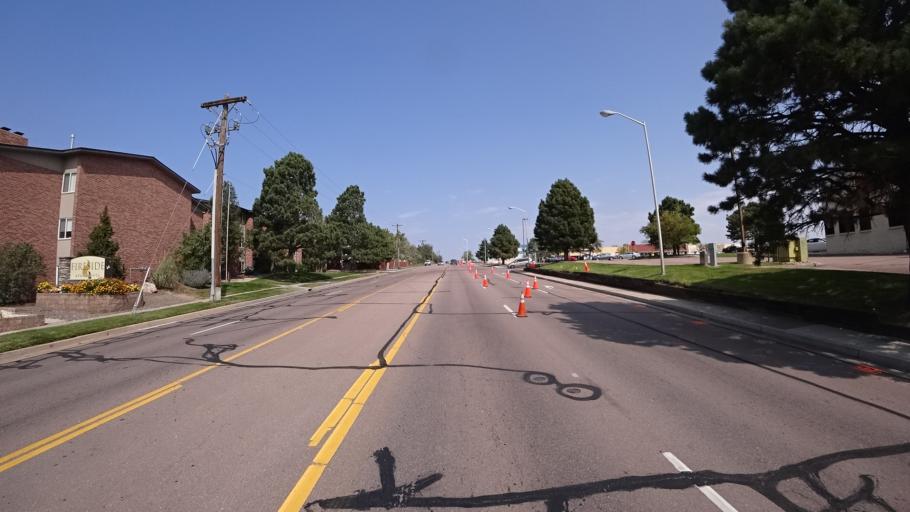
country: US
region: Colorado
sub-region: El Paso County
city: Cimarron Hills
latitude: 38.8415
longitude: -104.7480
